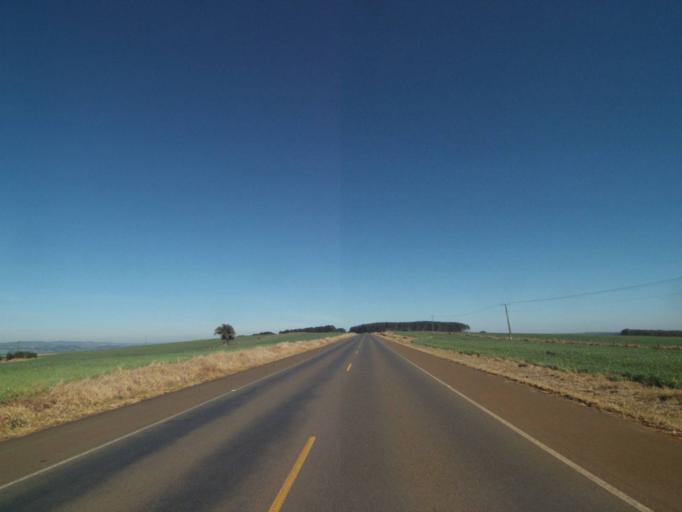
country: BR
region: Parana
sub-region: Tibagi
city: Tibagi
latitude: -24.4298
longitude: -50.4067
